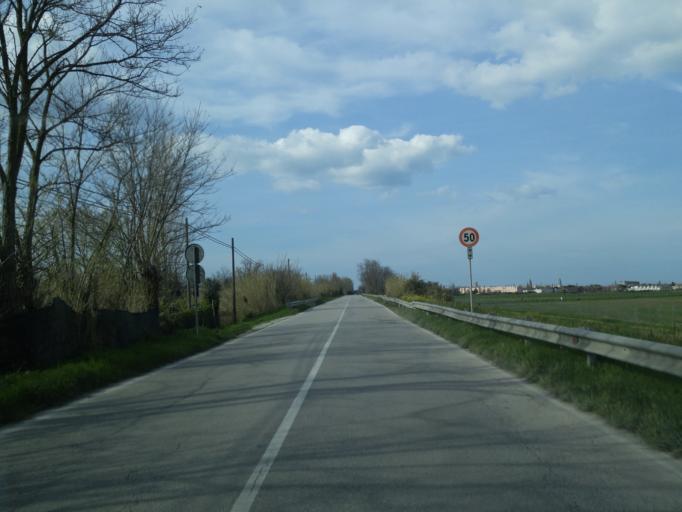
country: IT
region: The Marches
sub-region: Provincia di Pesaro e Urbino
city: Rosciano
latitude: 43.8202
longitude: 13.0169
